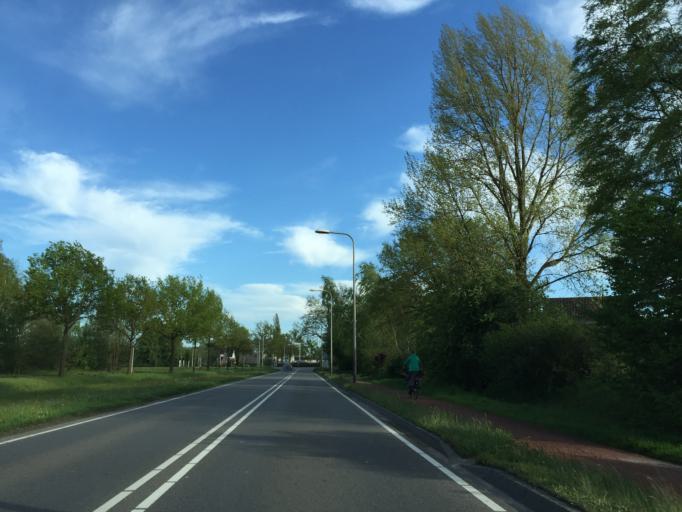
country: NL
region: Overijssel
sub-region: Gemeente Dalfsen
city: Dalfsen
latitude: 52.5145
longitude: 6.2603
